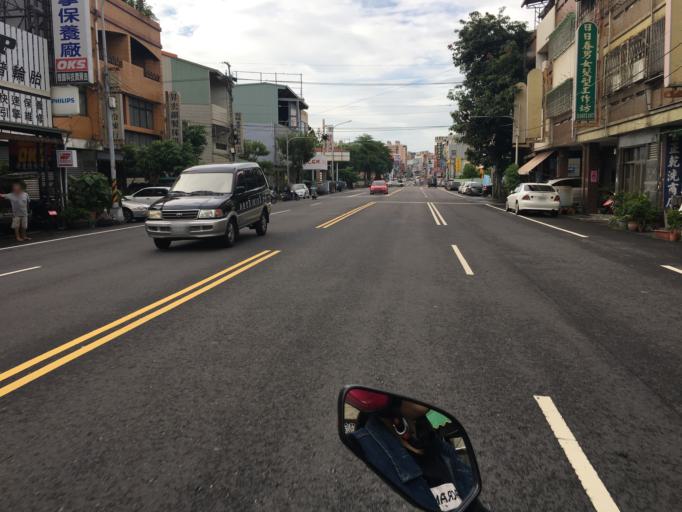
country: TW
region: Taiwan
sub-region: Taichung City
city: Taichung
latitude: 24.0982
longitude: 120.6872
